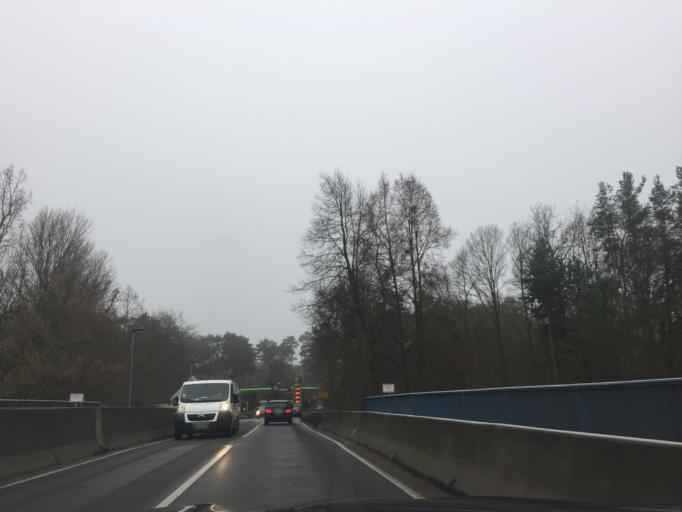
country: DE
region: Brandenburg
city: Falkensee
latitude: 52.6085
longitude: 13.1211
